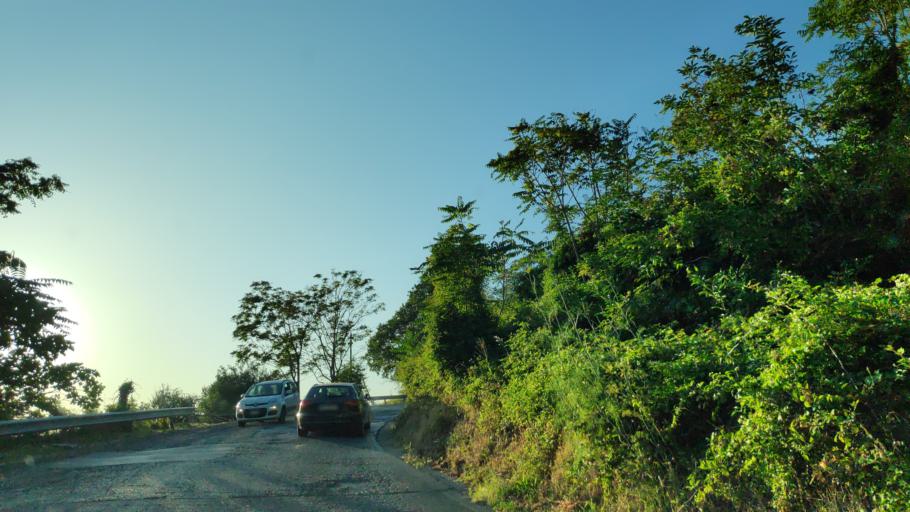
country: IT
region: Campania
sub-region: Provincia di Salerno
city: Corbara
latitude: 40.7224
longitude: 14.6021
